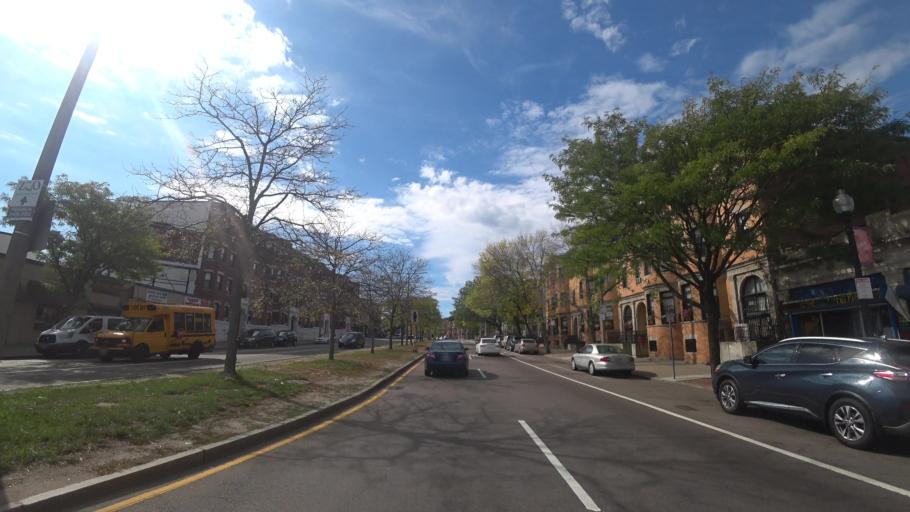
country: US
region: Massachusetts
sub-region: Suffolk County
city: Jamaica Plain
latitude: 42.3087
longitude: -71.0832
